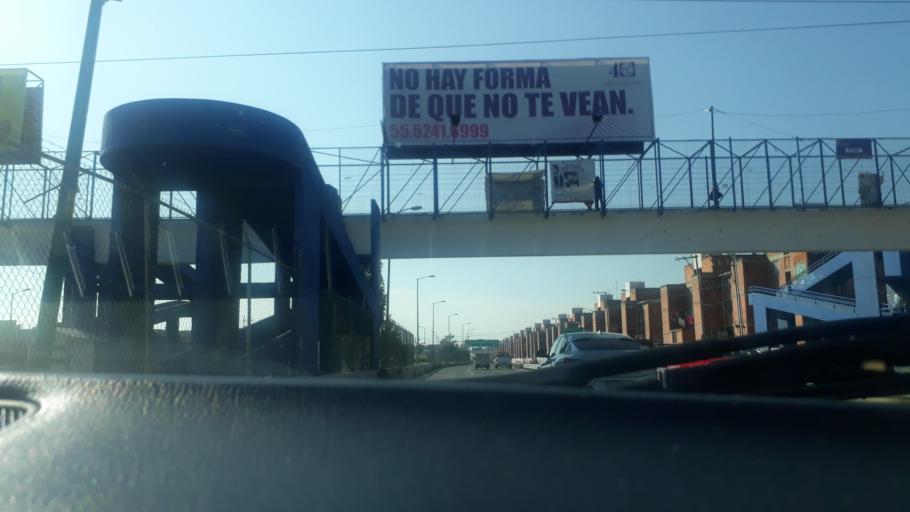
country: MX
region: Puebla
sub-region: Puebla
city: El Capulo (La Quebradora)
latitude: 18.9886
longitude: -98.2387
